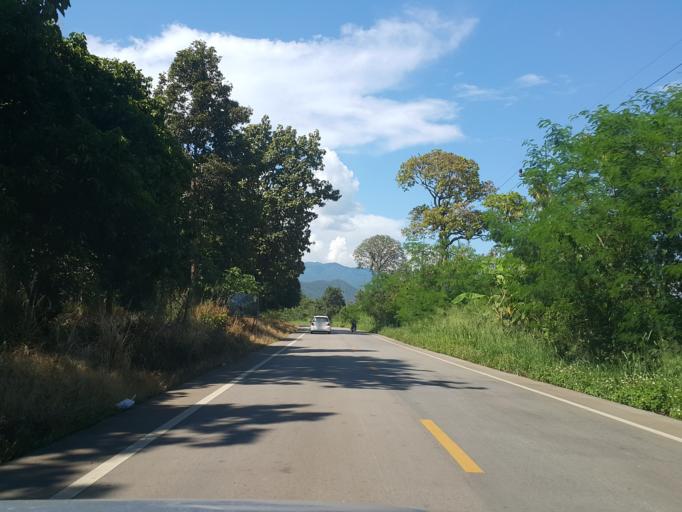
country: TH
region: Chiang Mai
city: Mae Taeng
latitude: 19.1546
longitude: 98.9430
